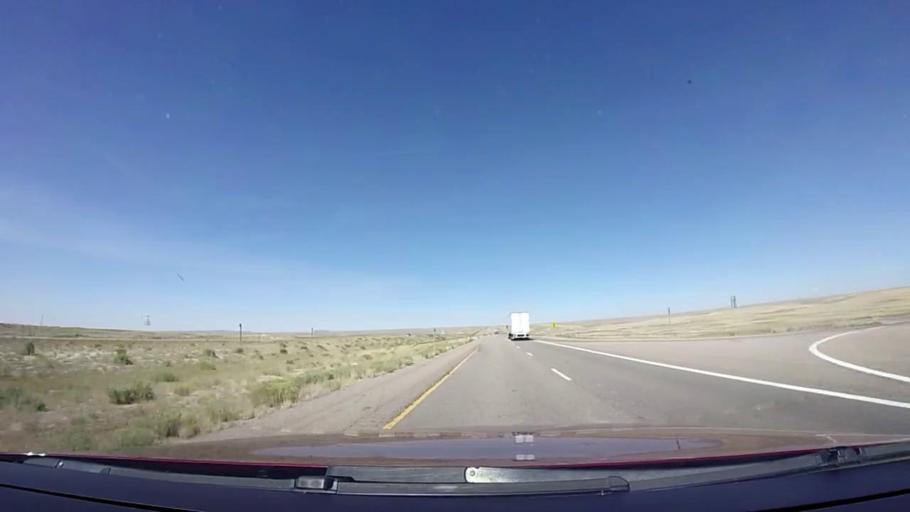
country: US
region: Wyoming
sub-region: Sweetwater County
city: Rock Springs
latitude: 41.6402
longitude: -108.4886
